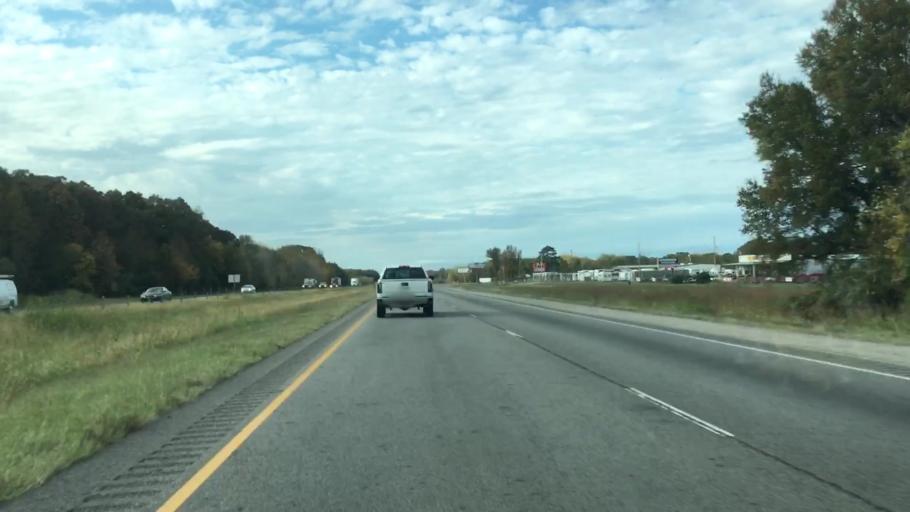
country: US
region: Arkansas
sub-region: Pope County
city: Atkins
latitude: 35.2205
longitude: -92.8313
